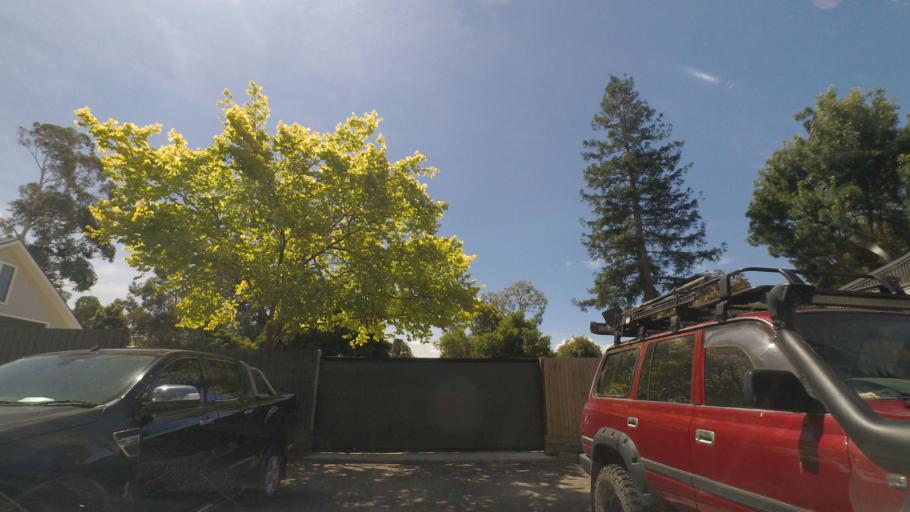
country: AU
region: Victoria
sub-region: Yarra Ranges
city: Montrose
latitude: -37.8061
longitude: 145.3456
